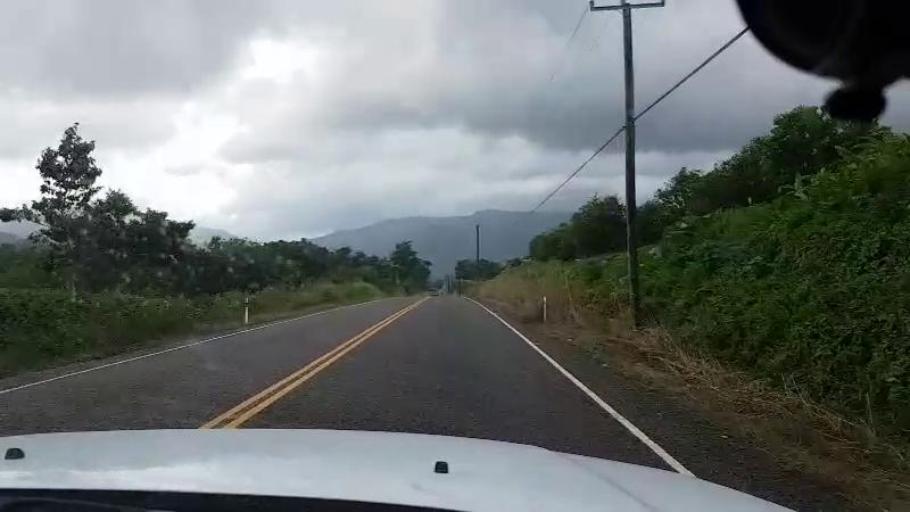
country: BZ
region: Cayo
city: Belmopan
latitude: 17.1164
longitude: -88.6561
